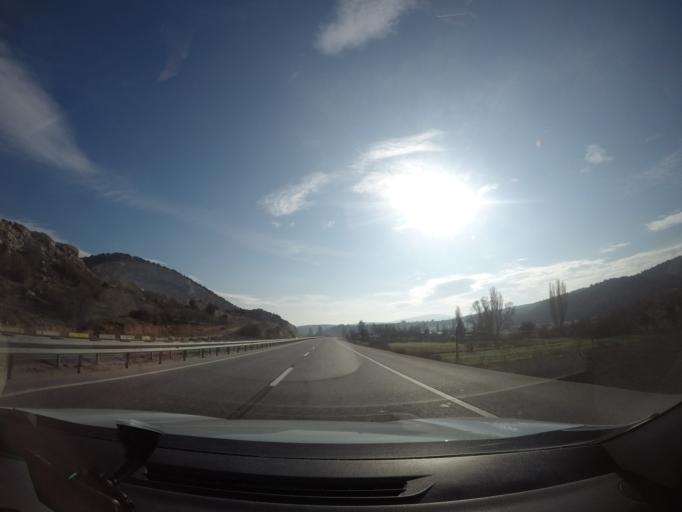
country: TR
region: Bilecik
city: Bozuyuk
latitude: 39.8943
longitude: 29.9639
